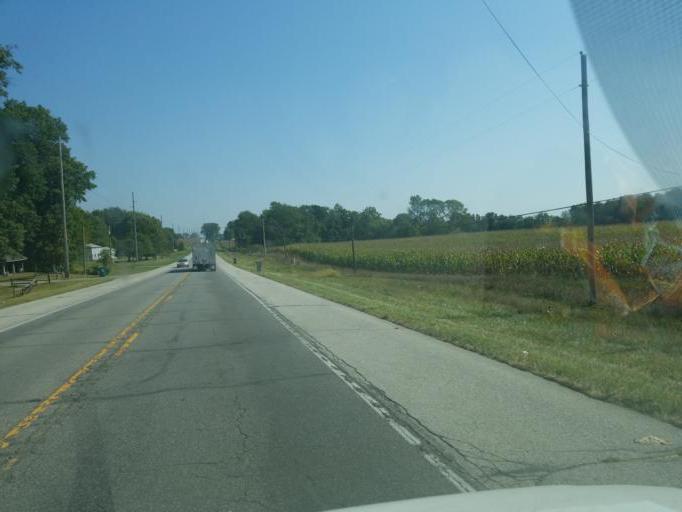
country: US
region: Indiana
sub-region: LaGrange County
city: Lagrange
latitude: 41.6418
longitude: -85.3002
